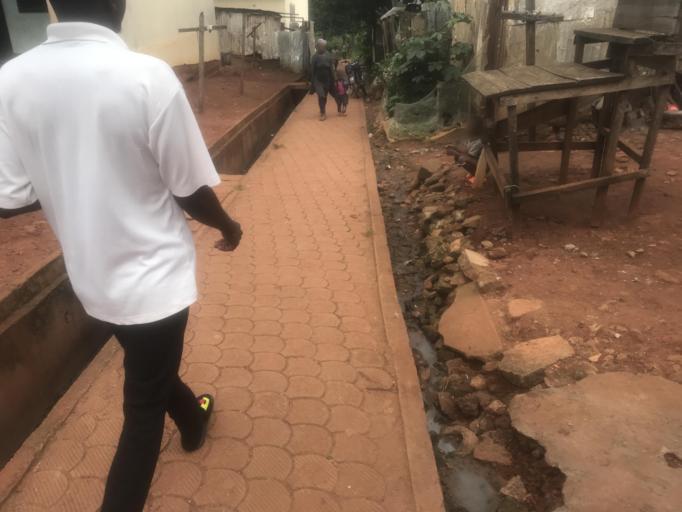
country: CM
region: Centre
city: Yaounde
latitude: 3.8530
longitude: 11.5050
